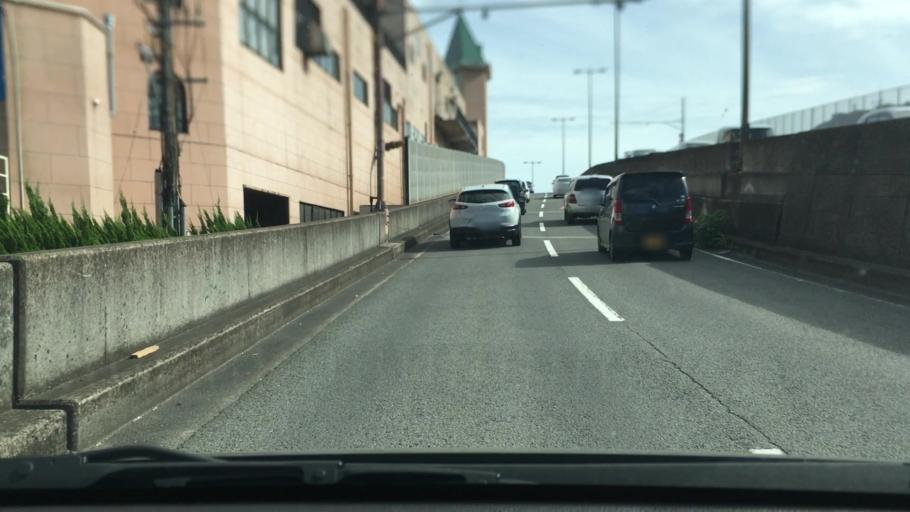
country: JP
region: Nagasaki
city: Nagasaki-shi
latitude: 32.7715
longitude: 129.8629
